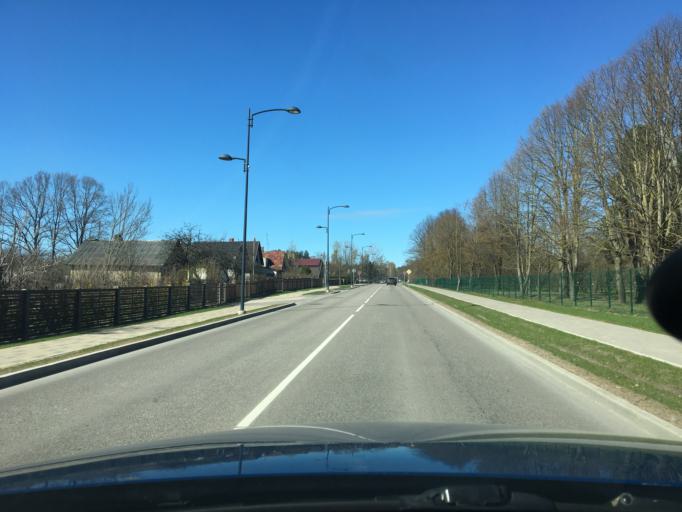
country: LV
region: Salaspils
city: Salaspils
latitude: 56.8641
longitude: 24.3514
